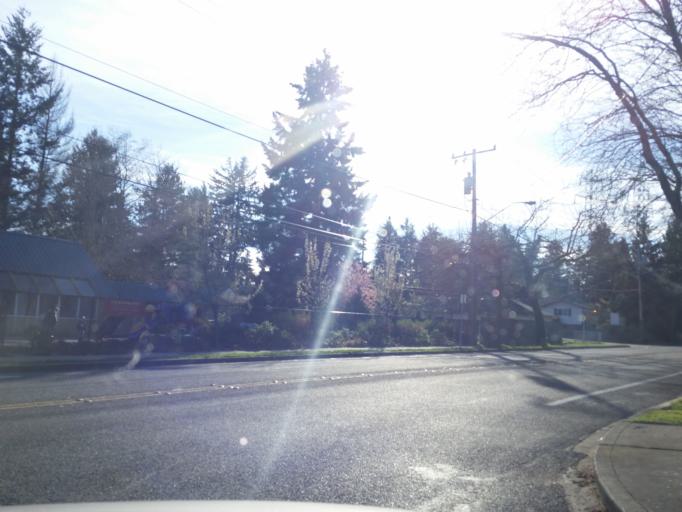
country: US
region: Washington
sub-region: King County
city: Shoreline
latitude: 47.7632
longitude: -122.3190
